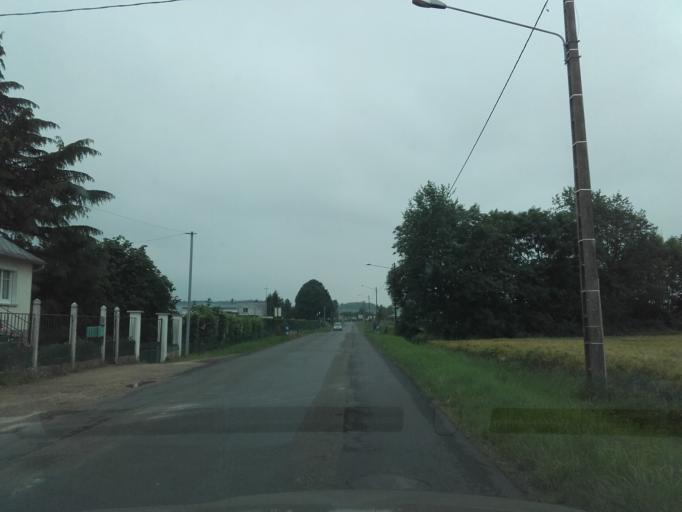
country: FR
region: Centre
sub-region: Departement du Loir-et-Cher
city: Montoire-sur-le-Loir
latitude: 47.7635
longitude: 0.8598
